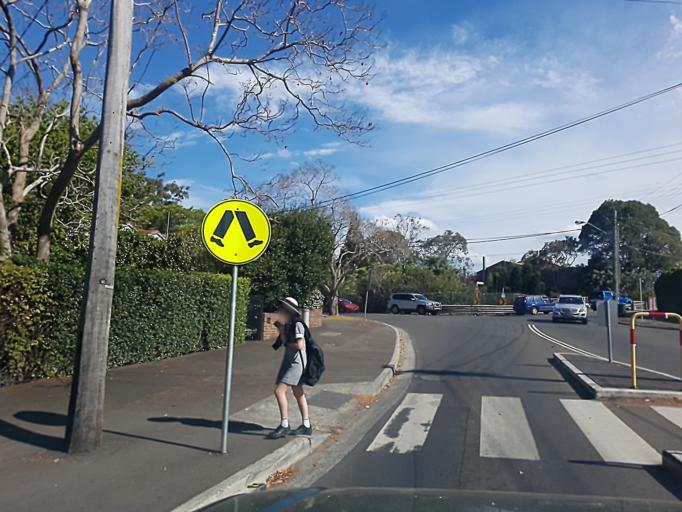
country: AU
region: New South Wales
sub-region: Ku-ring-gai
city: North Wahroonga
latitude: -33.7175
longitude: 151.1180
